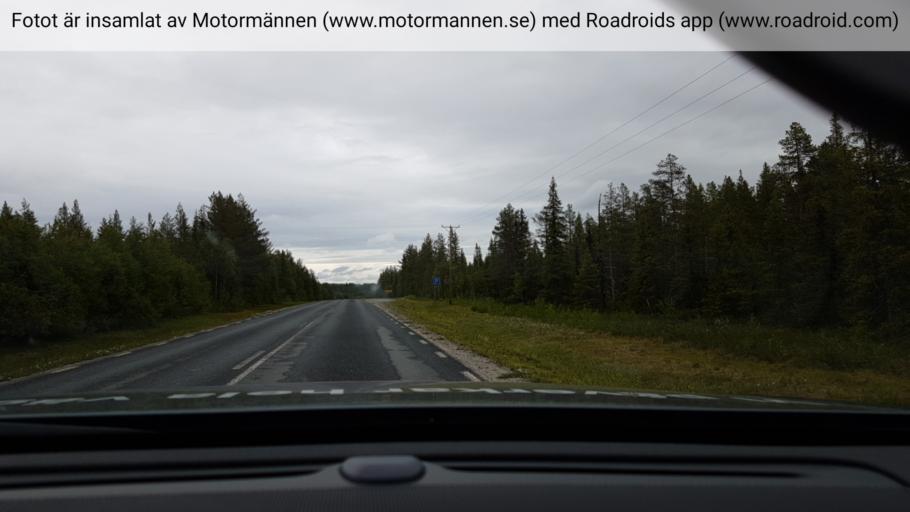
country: SE
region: Vaesterbotten
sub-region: Lycksele Kommun
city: Soderfors
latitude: 64.4646
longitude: 18.1645
